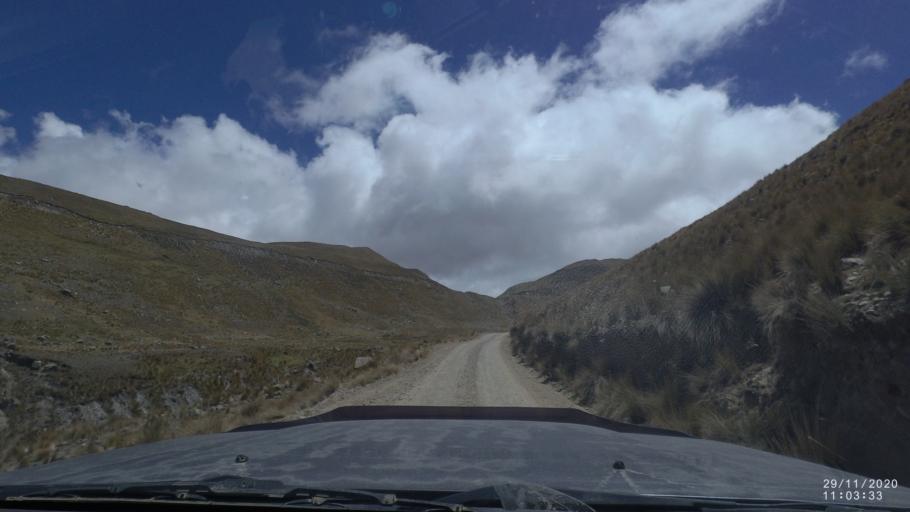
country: BO
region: Cochabamba
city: Cochabamba
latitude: -17.1891
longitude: -66.2216
